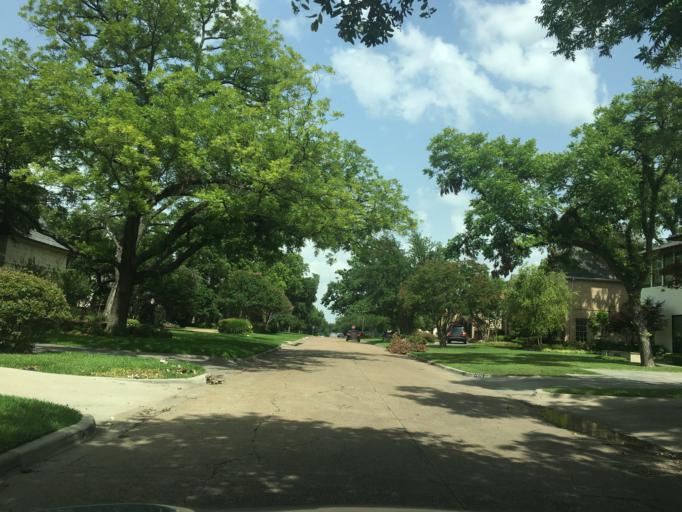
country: US
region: Texas
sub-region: Dallas County
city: University Park
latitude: 32.8884
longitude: -96.7918
